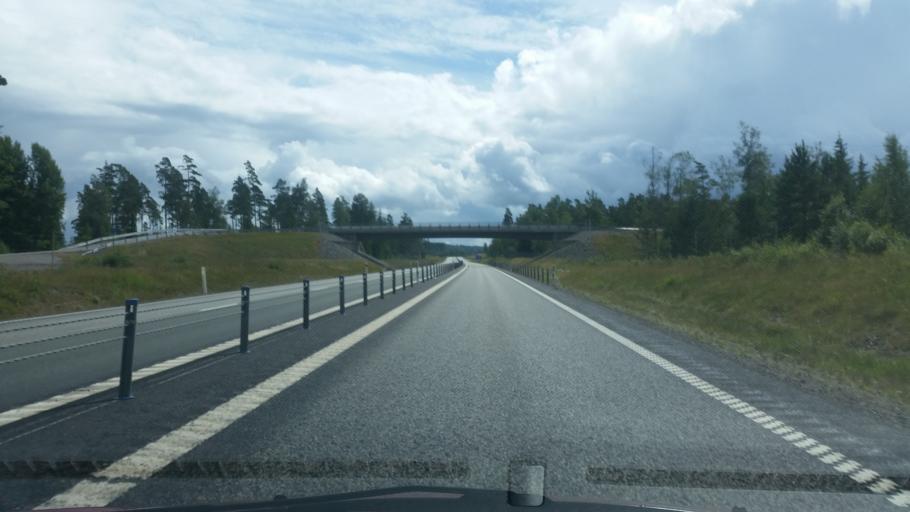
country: SE
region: Joenkoeping
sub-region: Gislaveds Kommun
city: Gislaved
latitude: 57.2906
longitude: 13.5955
